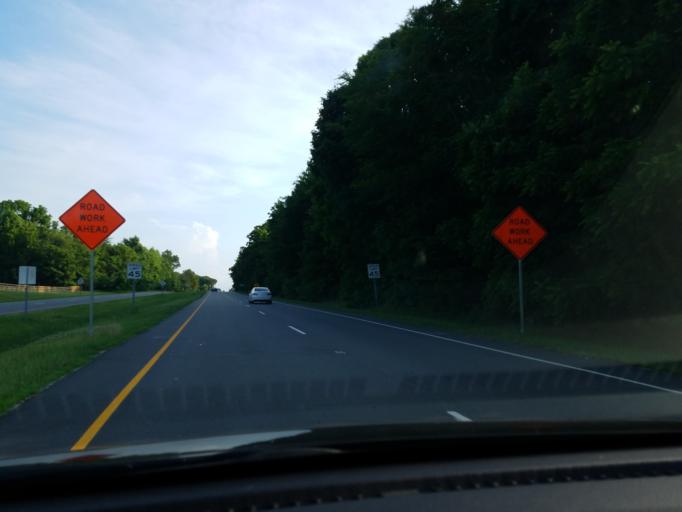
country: US
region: North Carolina
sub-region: Durham County
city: Gorman
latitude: 36.1205
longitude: -78.9019
